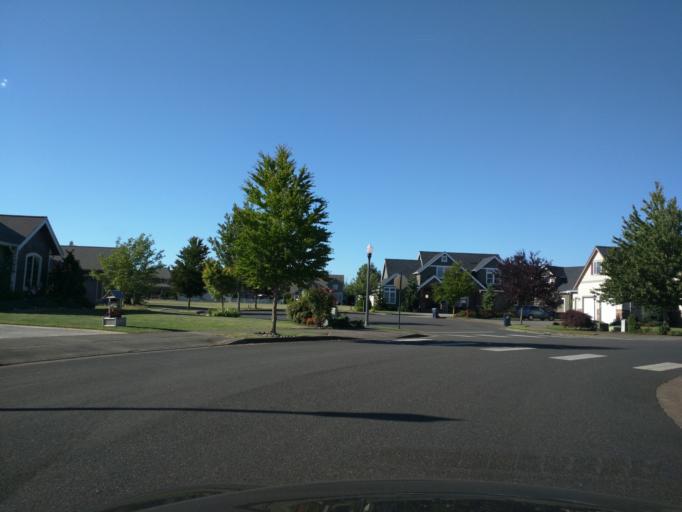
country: US
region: Washington
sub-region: Whatcom County
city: Lynden
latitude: 48.9548
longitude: -122.4604
